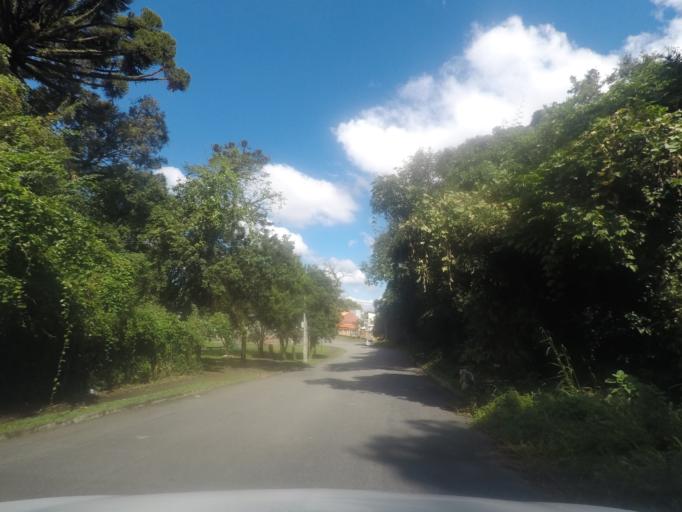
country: BR
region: Parana
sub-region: Pinhais
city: Pinhais
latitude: -25.4773
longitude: -49.2211
